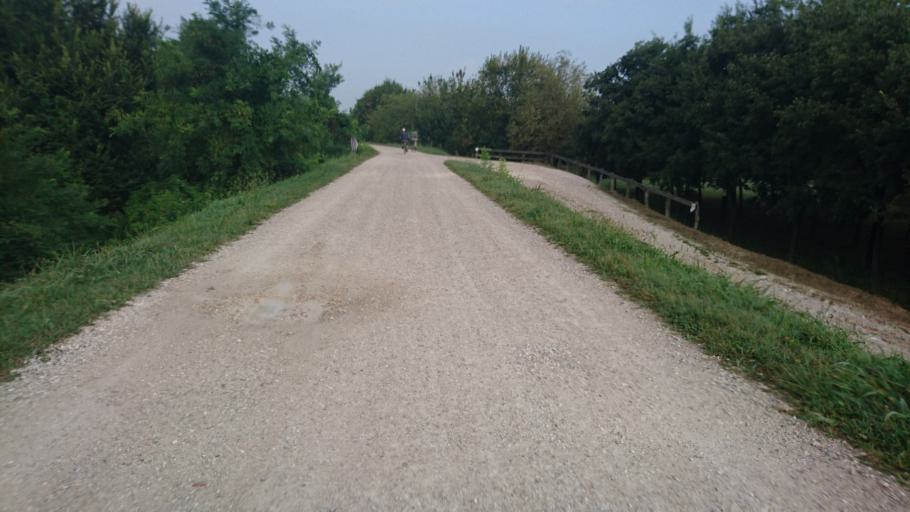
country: IT
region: Veneto
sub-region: Provincia di Padova
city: Selvazzano Dentro
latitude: 45.3968
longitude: 11.7947
